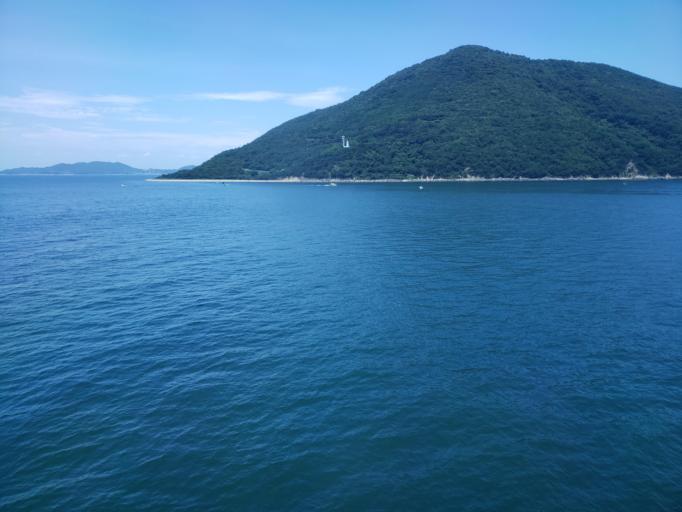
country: JP
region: Kagawa
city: Tonosho
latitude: 34.4077
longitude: 134.2391
